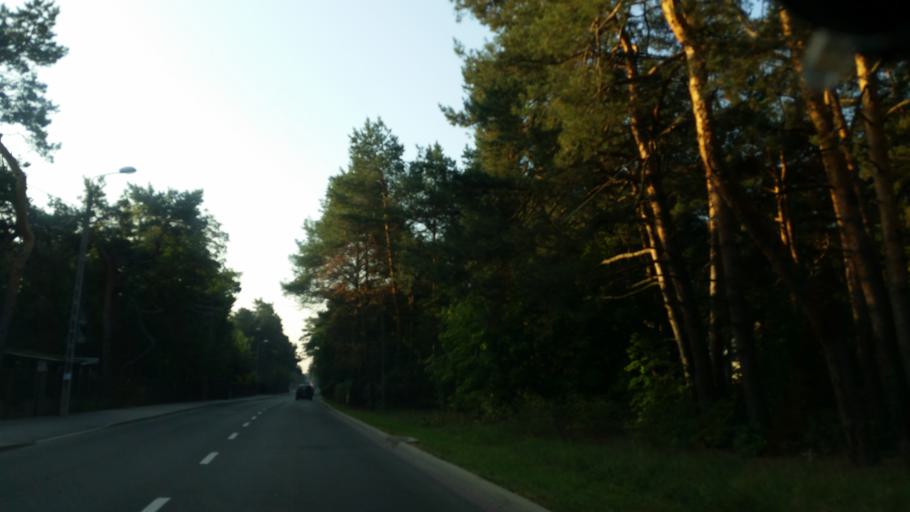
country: PL
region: Masovian Voivodeship
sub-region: Powiat otwocki
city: Jozefow
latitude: 52.1409
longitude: 21.2156
